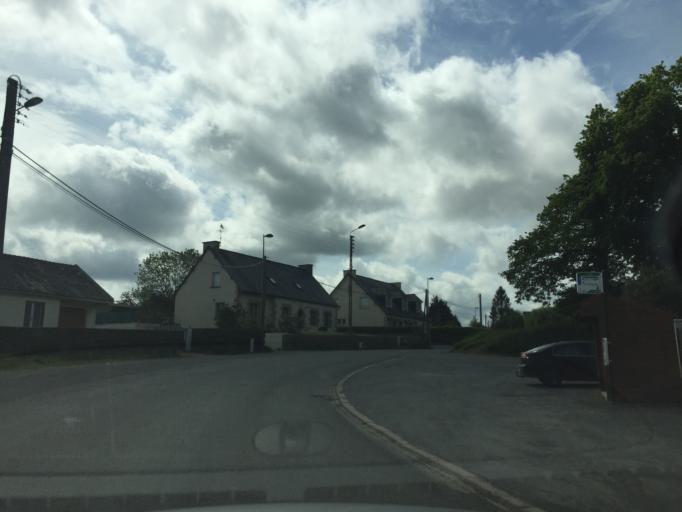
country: FR
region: Brittany
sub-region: Departement des Cotes-d'Armor
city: Corseul
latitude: 48.5105
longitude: -2.1265
